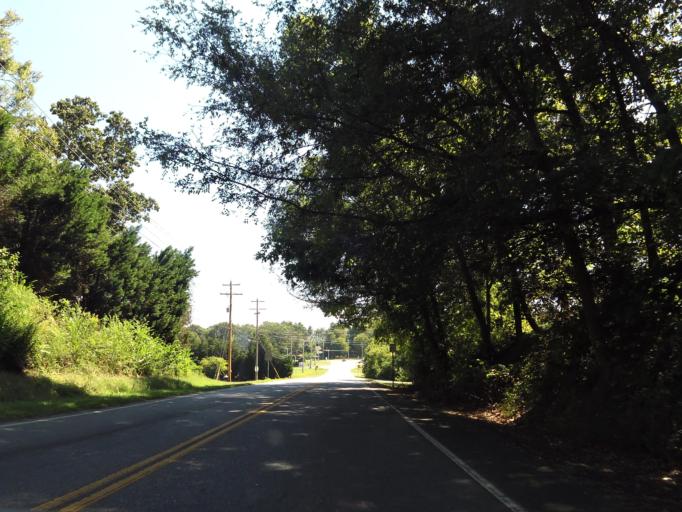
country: US
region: Tennessee
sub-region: Blount County
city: Eagleton Village
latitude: 35.8010
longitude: -83.9475
